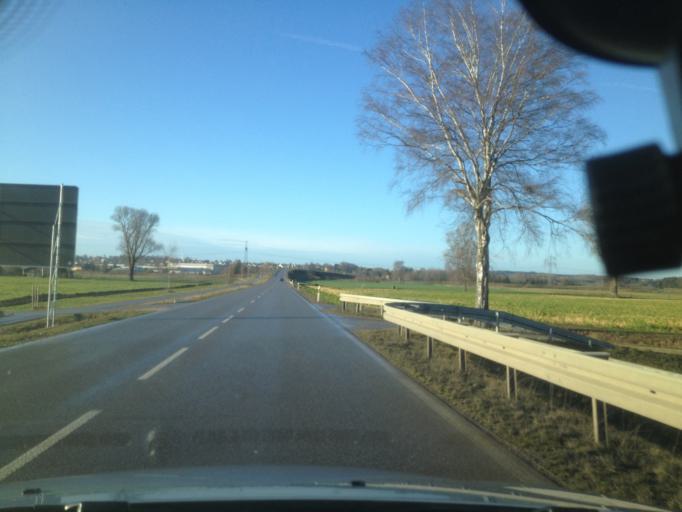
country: DE
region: Bavaria
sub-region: Swabia
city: Burgau
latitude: 48.4435
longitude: 10.4250
